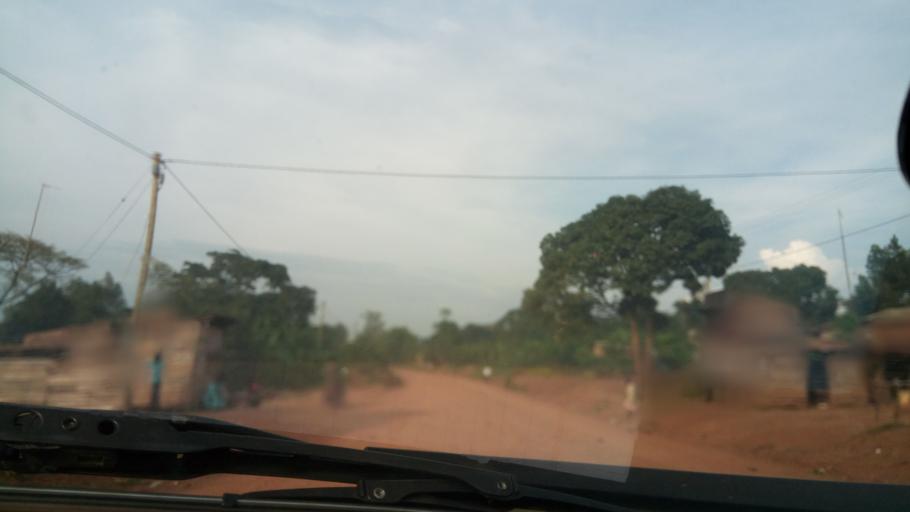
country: UG
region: Central Region
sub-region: Mityana District
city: Mityana
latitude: 0.5268
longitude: 32.1639
